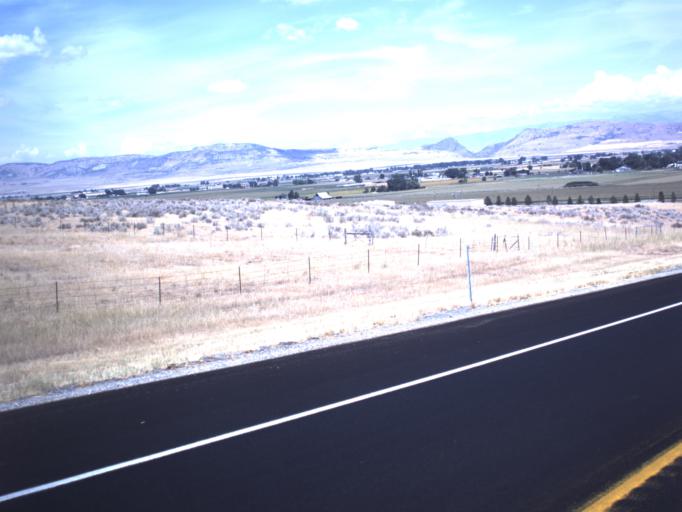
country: US
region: Utah
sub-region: Box Elder County
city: Garland
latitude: 41.7846
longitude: -112.1715
